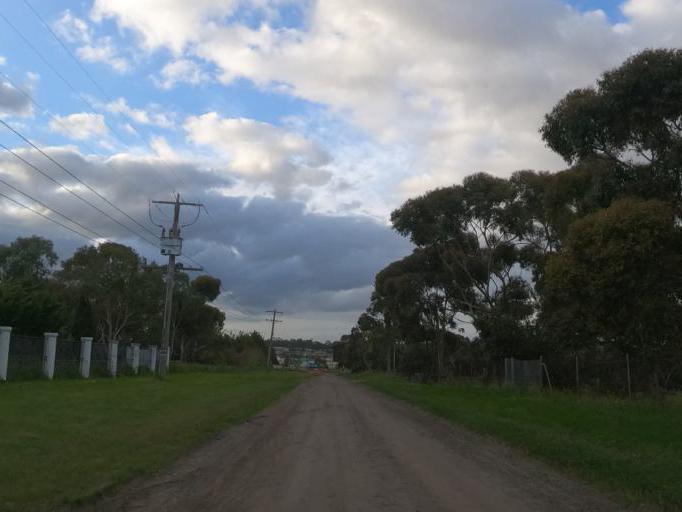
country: AU
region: Victoria
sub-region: Hume
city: Greenvale
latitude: -37.6334
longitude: 144.8900
